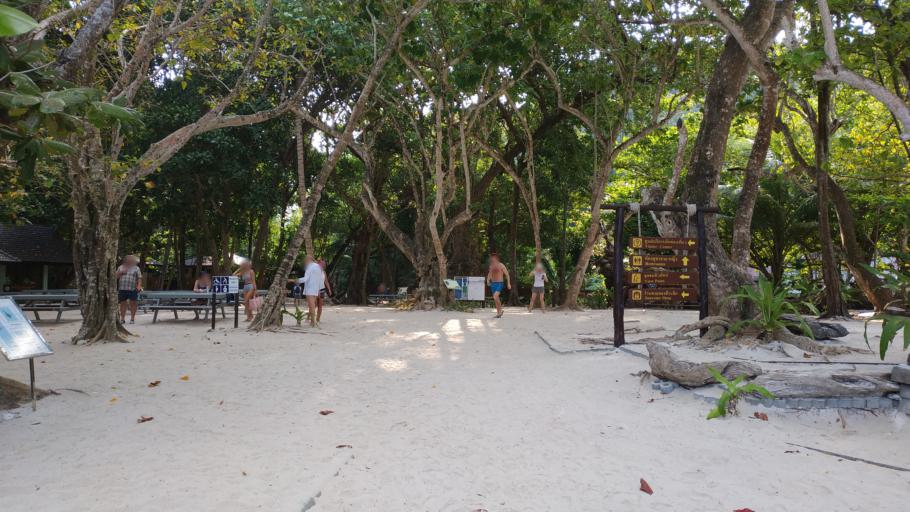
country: TH
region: Phangnga
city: Ban Khao Lak
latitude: 8.6658
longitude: 97.6484
